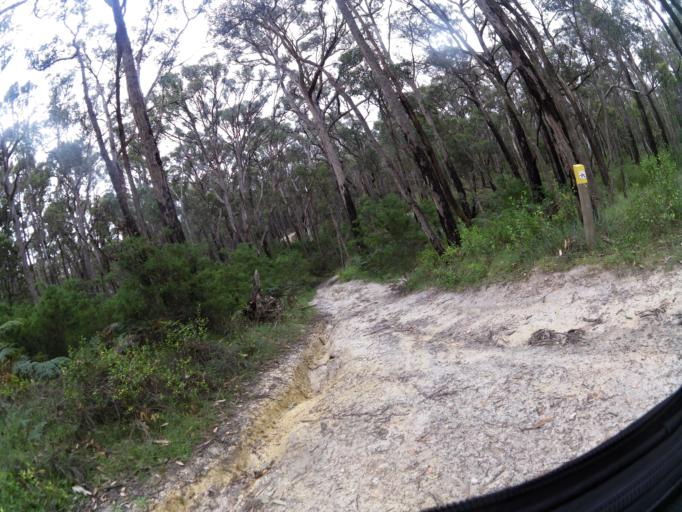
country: AU
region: Victoria
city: Brown Hill
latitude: -37.4940
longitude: 143.9086
